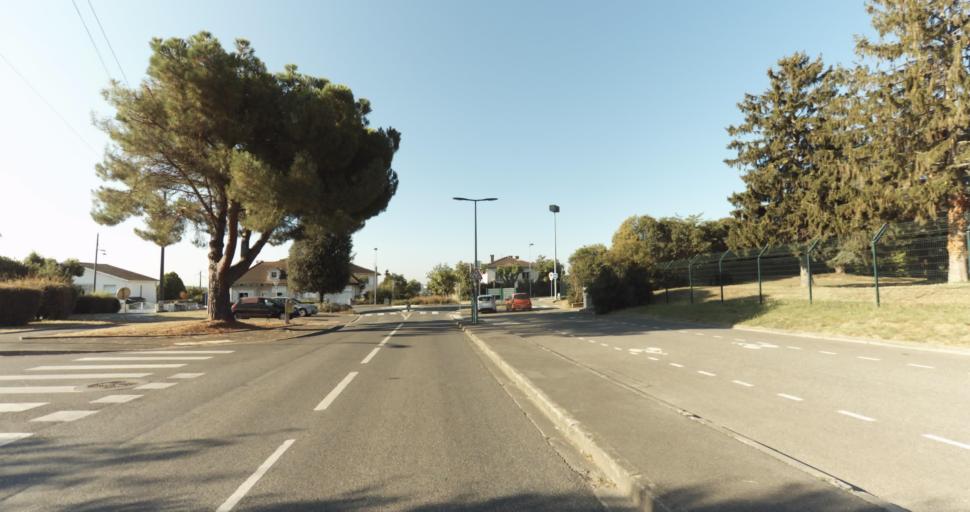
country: FR
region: Midi-Pyrenees
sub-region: Departement de la Haute-Garonne
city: L'Union
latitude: 43.6545
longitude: 1.4915
